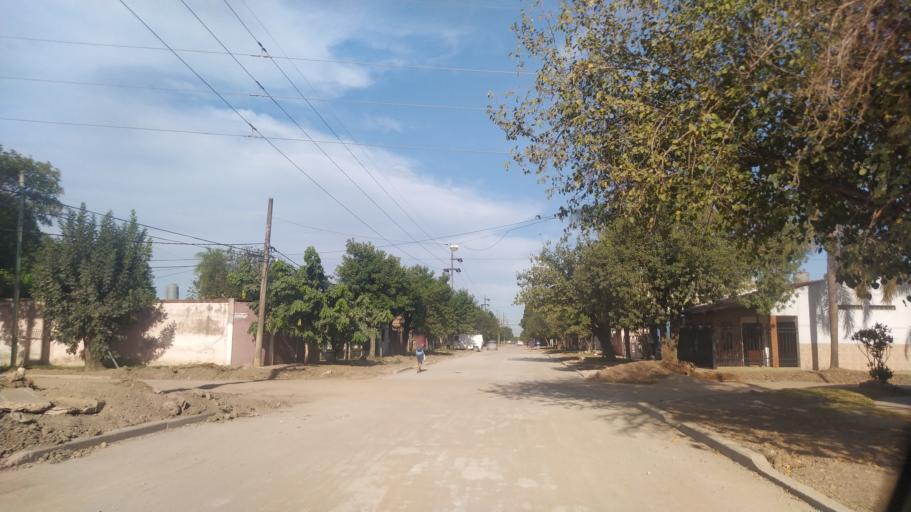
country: AR
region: Corrientes
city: Corrientes
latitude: -27.4805
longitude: -58.8103
